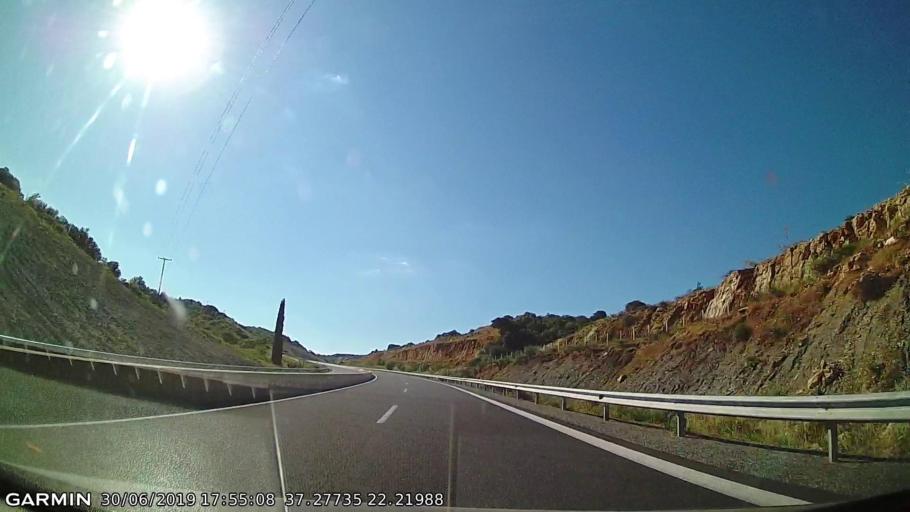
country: GR
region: Peloponnese
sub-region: Nomos Arkadias
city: Megalopoli
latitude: 37.2777
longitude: 22.2195
